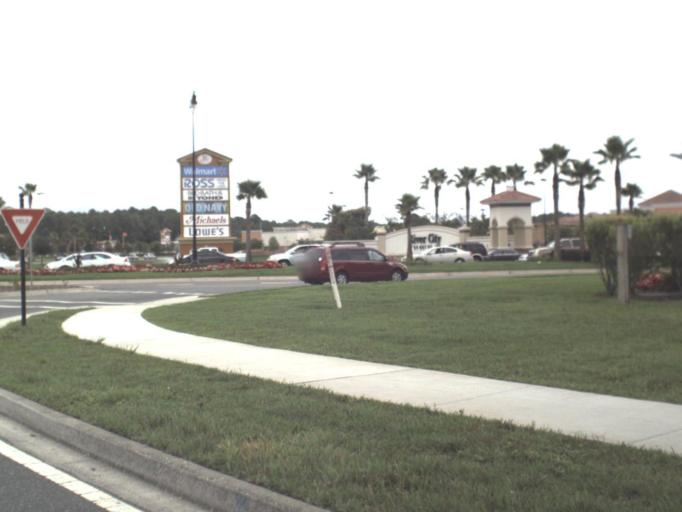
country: US
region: Florida
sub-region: Duval County
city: Jacksonville
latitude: 30.4812
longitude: -81.6397
